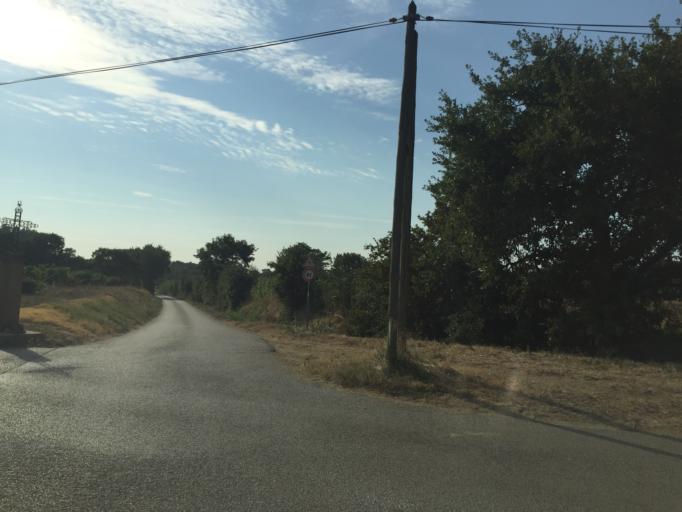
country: FR
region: Provence-Alpes-Cote d'Azur
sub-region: Departement du Vaucluse
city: Courthezon
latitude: 44.0810
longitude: 4.8608
